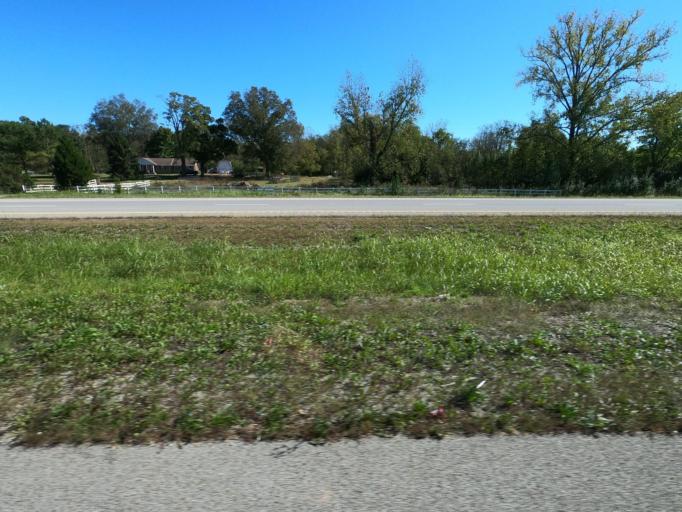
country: US
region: Tennessee
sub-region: Maury County
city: Mount Pleasant
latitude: 35.5005
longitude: -87.2325
